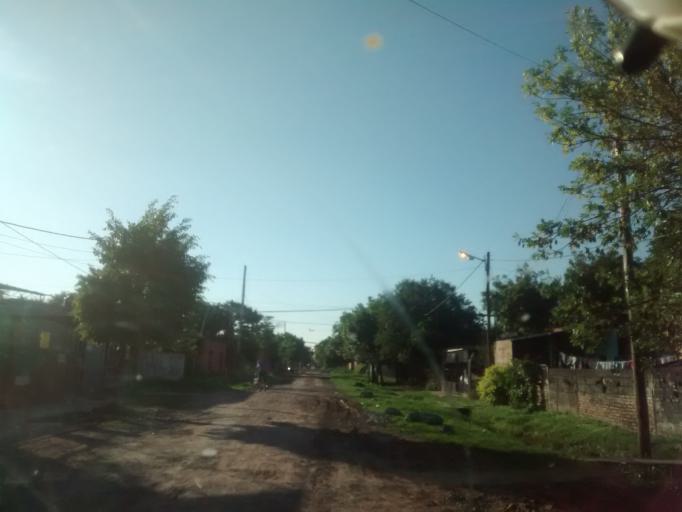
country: AR
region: Chaco
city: Resistencia
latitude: -27.4496
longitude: -59.0069
